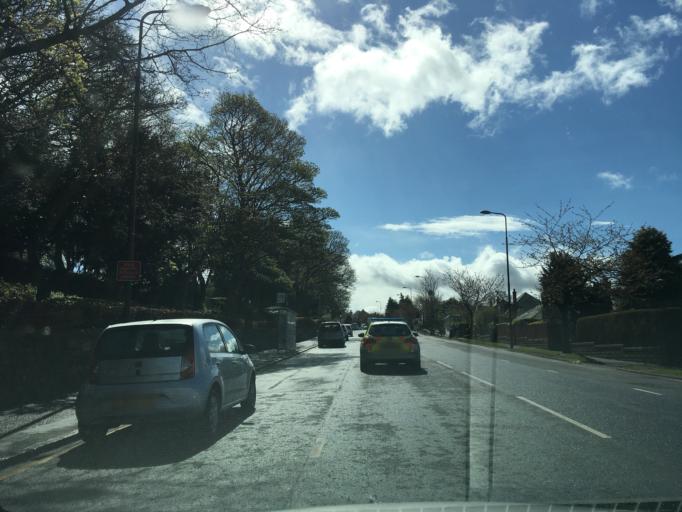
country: GB
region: Scotland
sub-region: Edinburgh
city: Colinton
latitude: 55.9195
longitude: -3.2406
